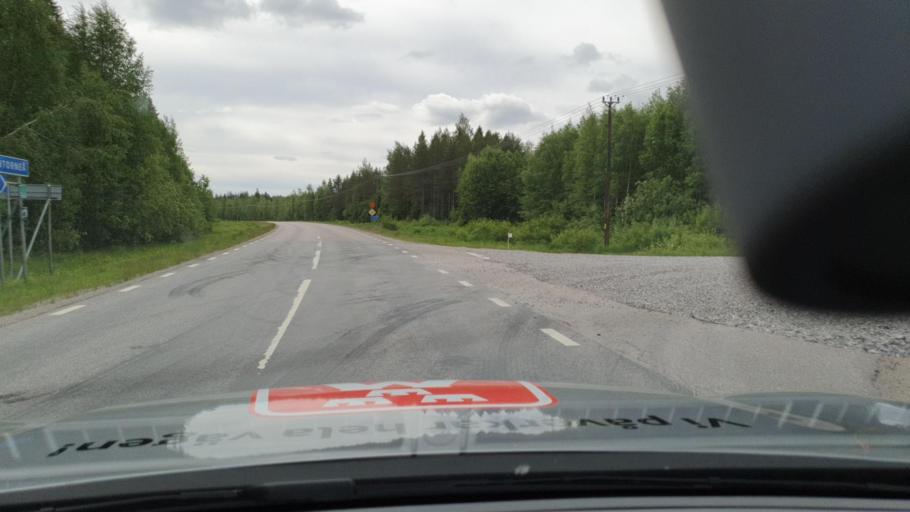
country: SE
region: Norrbotten
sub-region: Kalix Kommun
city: Kalix
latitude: 65.9126
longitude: 23.4553
